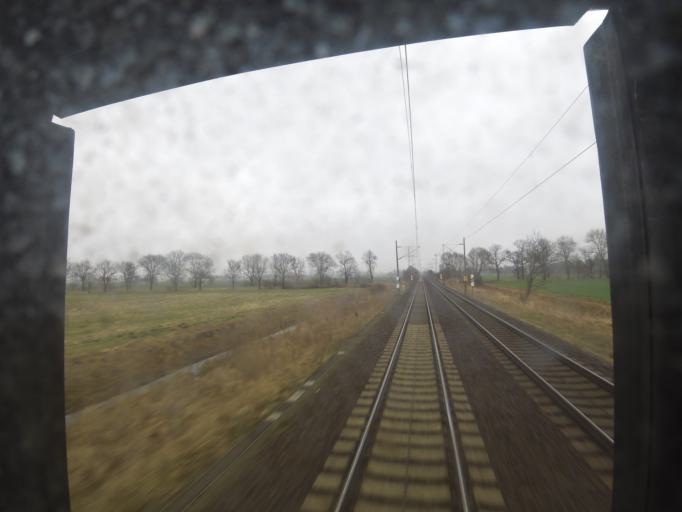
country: DE
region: Brandenburg
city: Nauen
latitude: 52.6251
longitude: 12.8488
